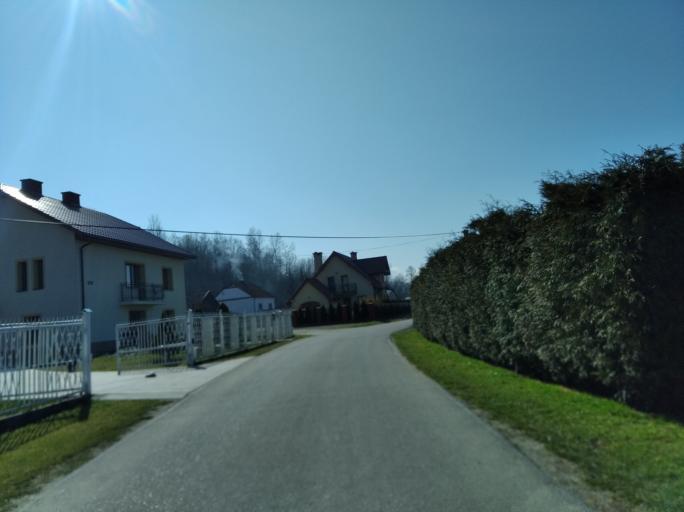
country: PL
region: Subcarpathian Voivodeship
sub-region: Powiat strzyzowski
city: Wysoka Strzyzowska
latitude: 49.8549
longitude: 21.7367
